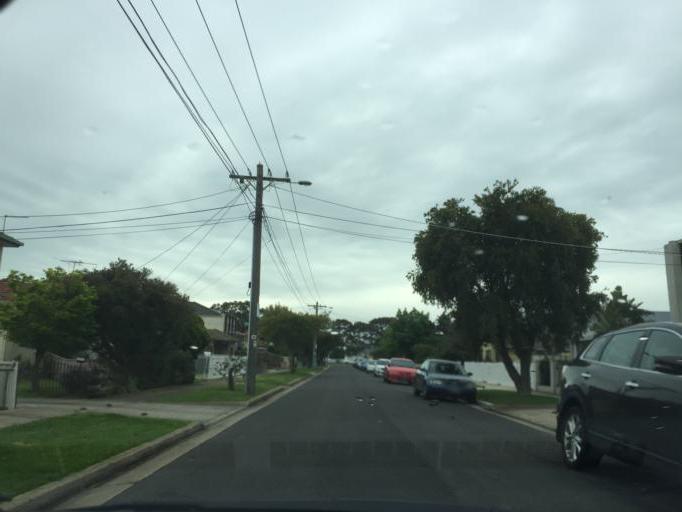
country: AU
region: Victoria
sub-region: Brimbank
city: Sunshine North
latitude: -37.7795
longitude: 144.8354
